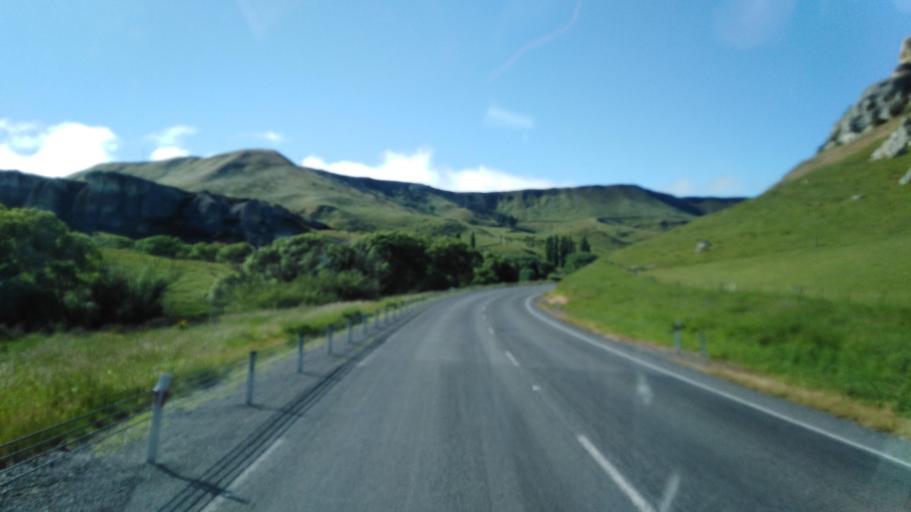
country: NZ
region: Canterbury
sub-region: Hurunui District
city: Amberley
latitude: -42.9825
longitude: 172.7176
